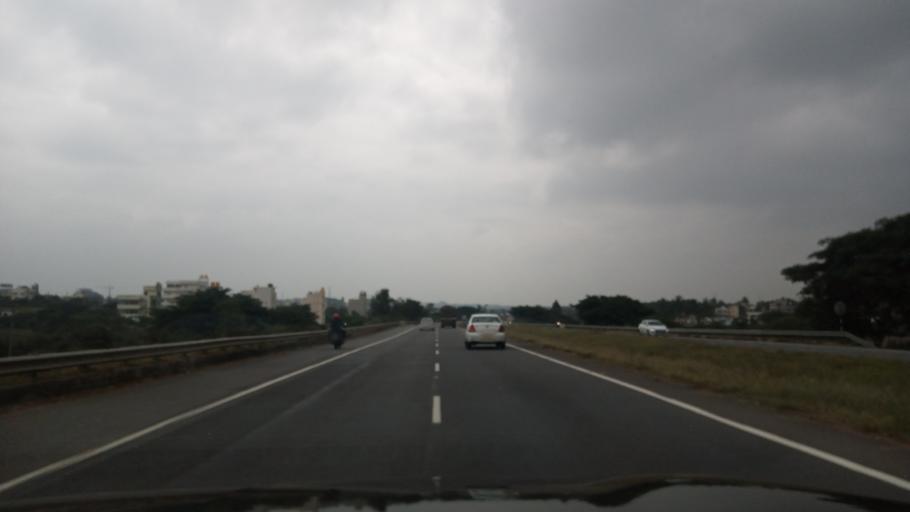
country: IN
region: Karnataka
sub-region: Bangalore Urban
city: Bangalore
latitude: 12.9592
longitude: 77.4715
